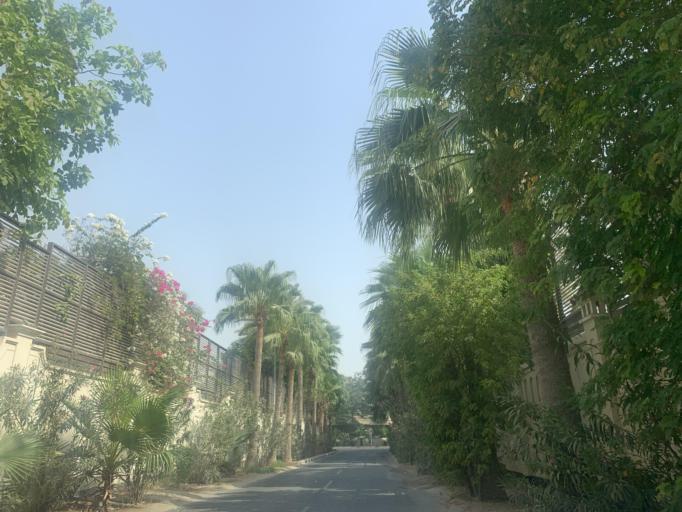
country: BH
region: Manama
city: Jidd Hafs
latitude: 26.2069
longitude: 50.4732
